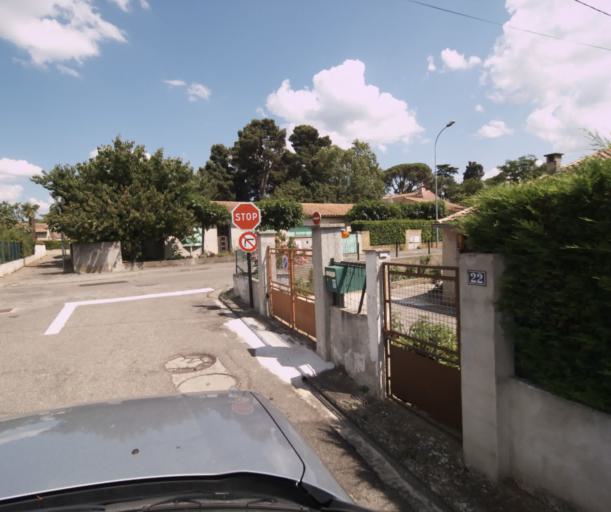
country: FR
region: Languedoc-Roussillon
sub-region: Departement de l'Aude
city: Limoux
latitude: 43.0593
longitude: 2.2196
